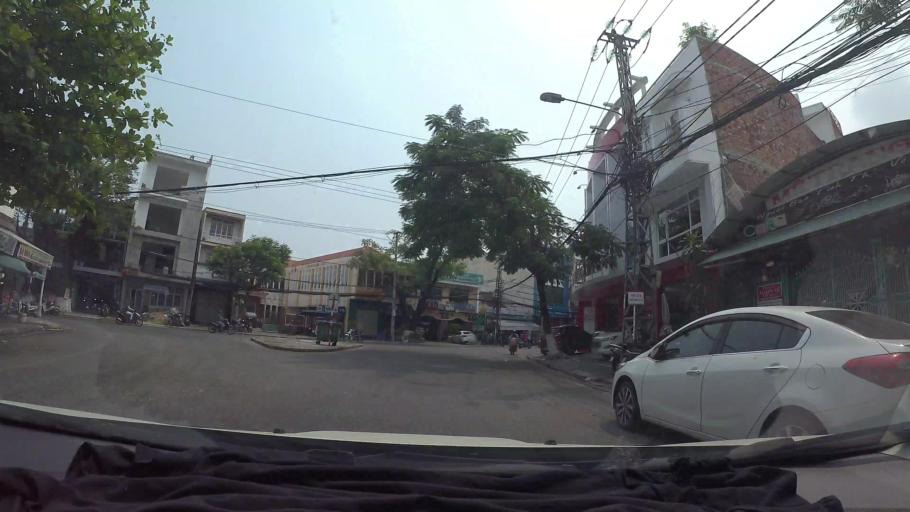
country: VN
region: Da Nang
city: Da Nang
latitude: 16.0543
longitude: 108.2190
